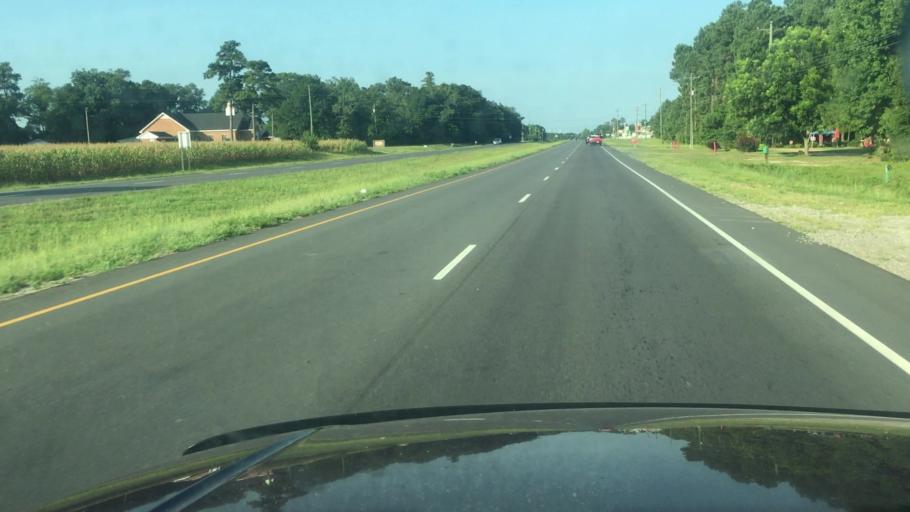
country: US
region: North Carolina
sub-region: Cumberland County
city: Hope Mills
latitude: 34.9338
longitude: -78.8498
